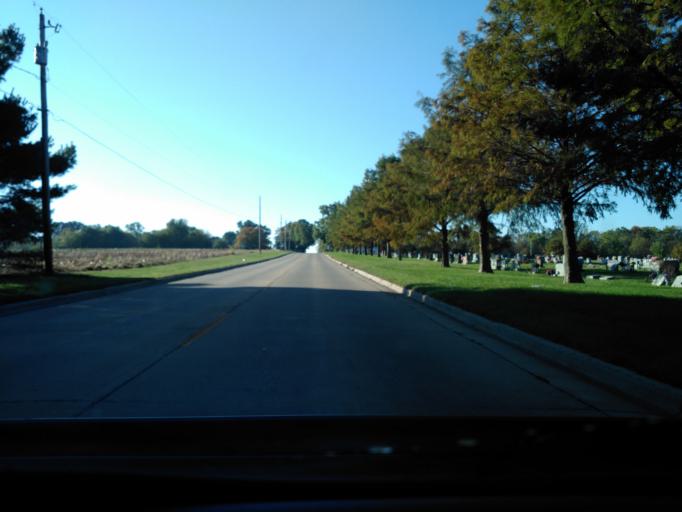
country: US
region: Illinois
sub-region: Bond County
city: Greenville
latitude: 38.8946
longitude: -89.3912
